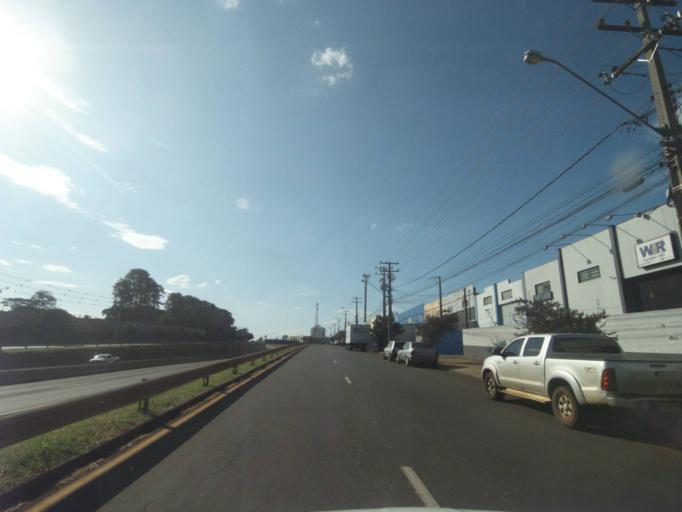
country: BR
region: Parana
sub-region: Londrina
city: Londrina
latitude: -23.3512
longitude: -51.1648
